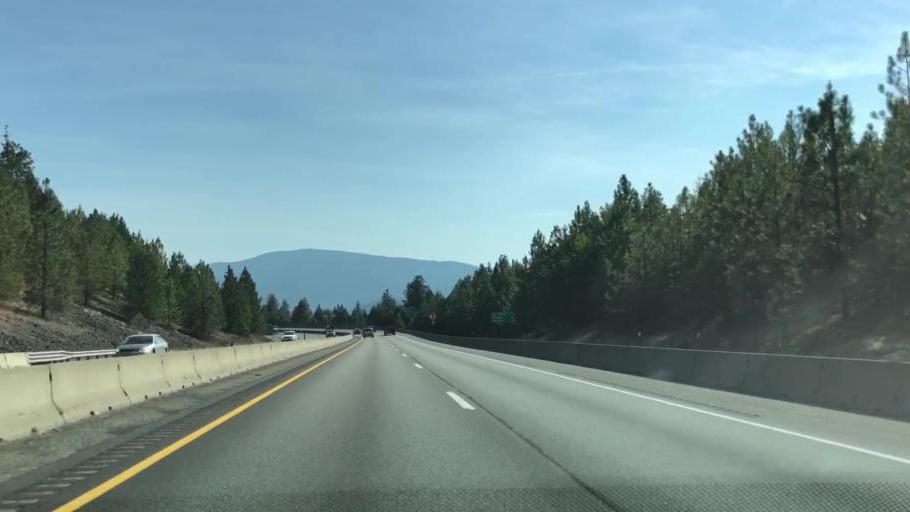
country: US
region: Idaho
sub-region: Kootenai County
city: Coeur d'Alene
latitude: 47.6442
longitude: -116.7136
